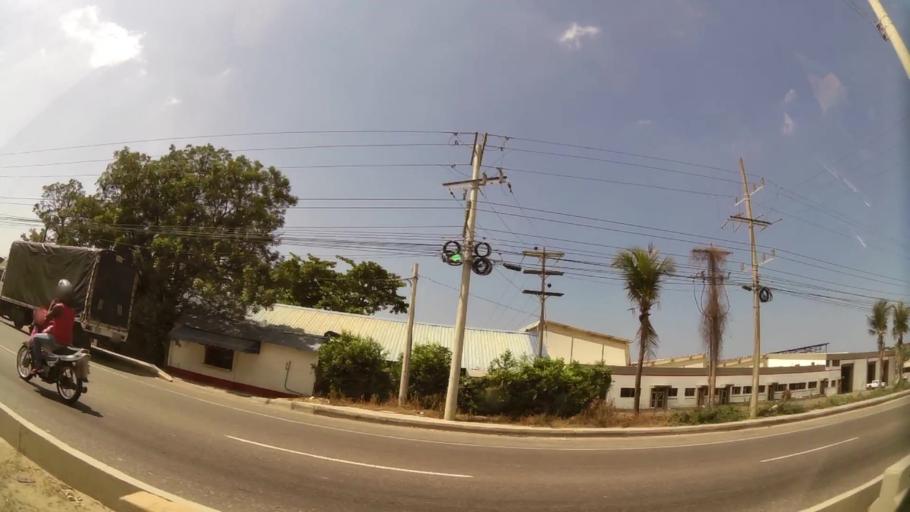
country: CO
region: Bolivar
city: Cartagena
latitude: 10.3660
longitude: -75.5078
